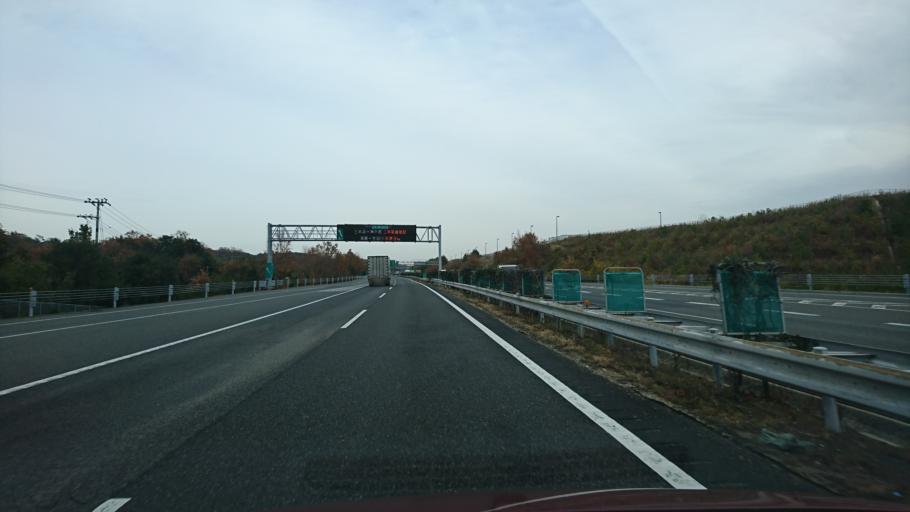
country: JP
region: Hyogo
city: Miki
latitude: 34.8031
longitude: 135.0678
